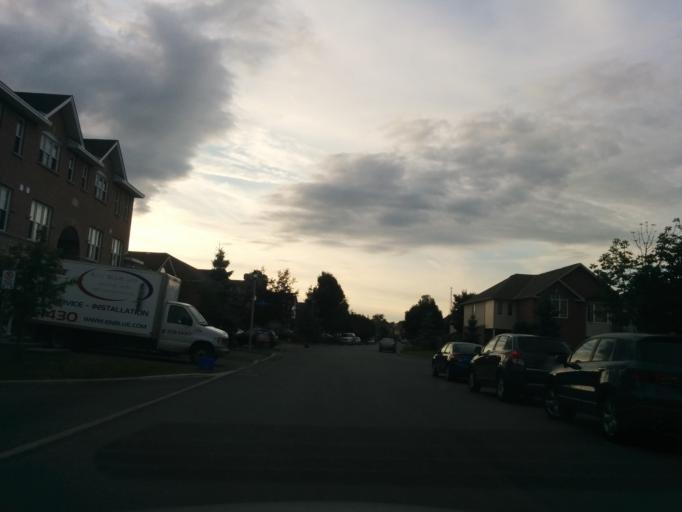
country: CA
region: Ontario
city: Ottawa
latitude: 45.3644
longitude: -75.7403
